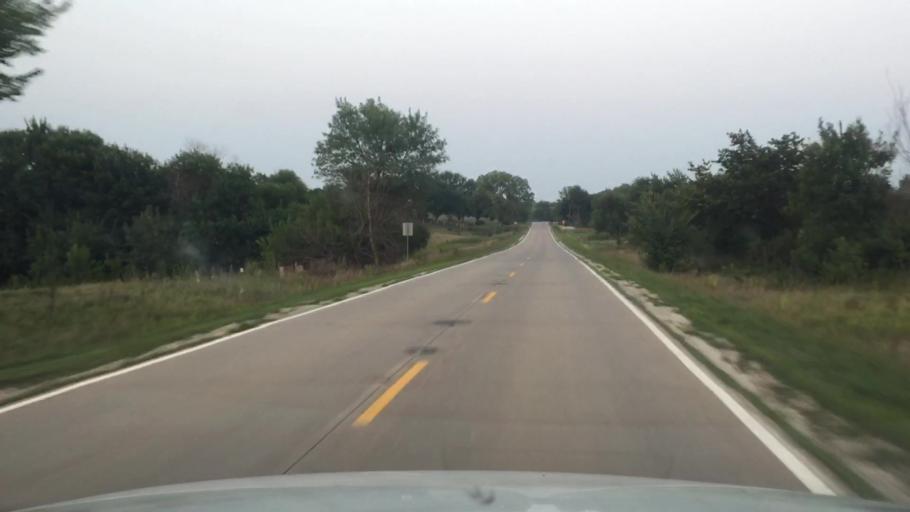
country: US
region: Iowa
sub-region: Clarke County
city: Osceola
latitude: 41.1802
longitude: -93.7198
